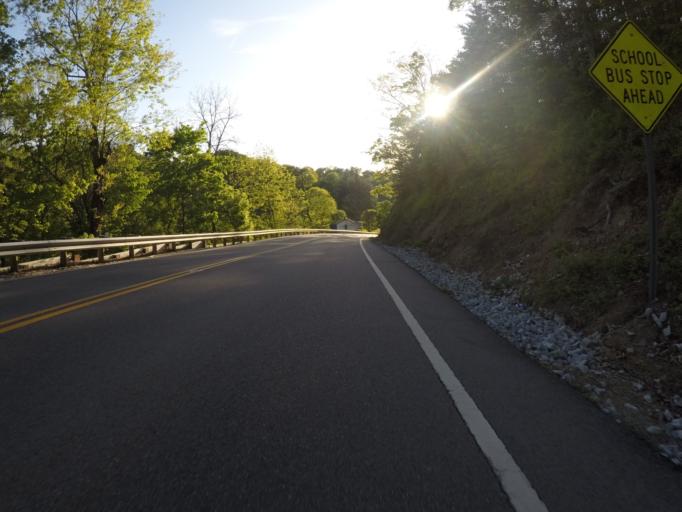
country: US
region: West Virginia
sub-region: Cabell County
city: Huntington
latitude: 38.5511
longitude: -82.4384
